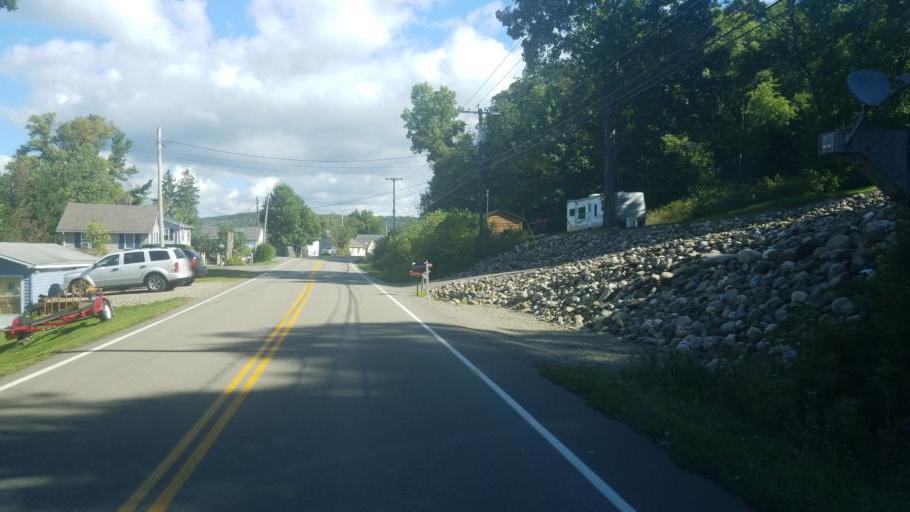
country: US
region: New York
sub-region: Allegany County
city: Cuba
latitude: 42.2421
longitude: -78.3025
